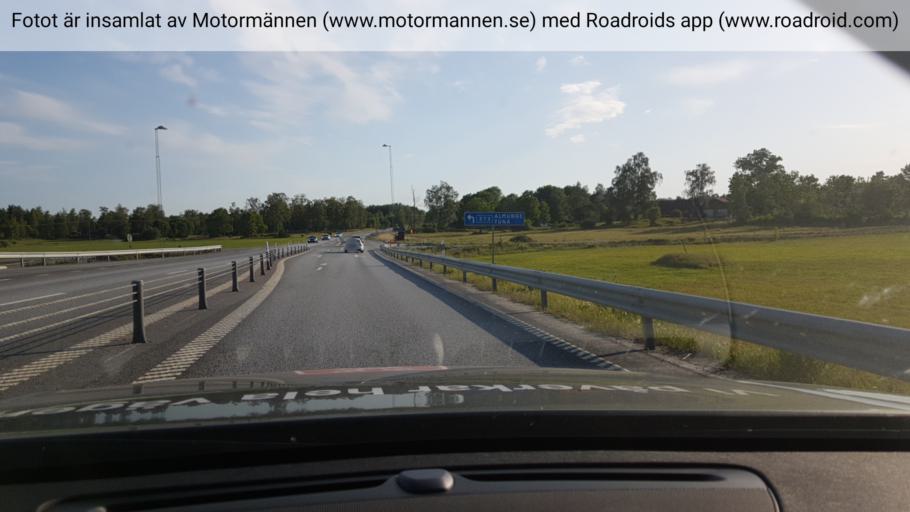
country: SE
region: Uppsala
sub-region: Osthammars Kommun
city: Gimo
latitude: 60.0372
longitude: 18.0348
